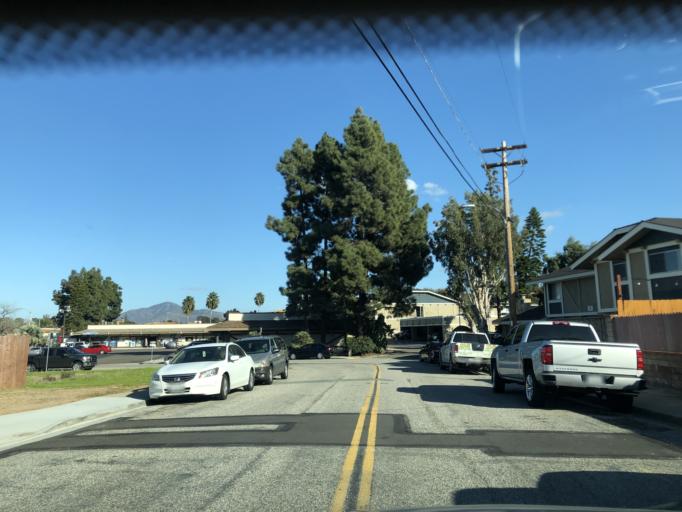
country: US
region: California
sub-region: San Diego County
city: Chula Vista
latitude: 32.6471
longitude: -117.0660
